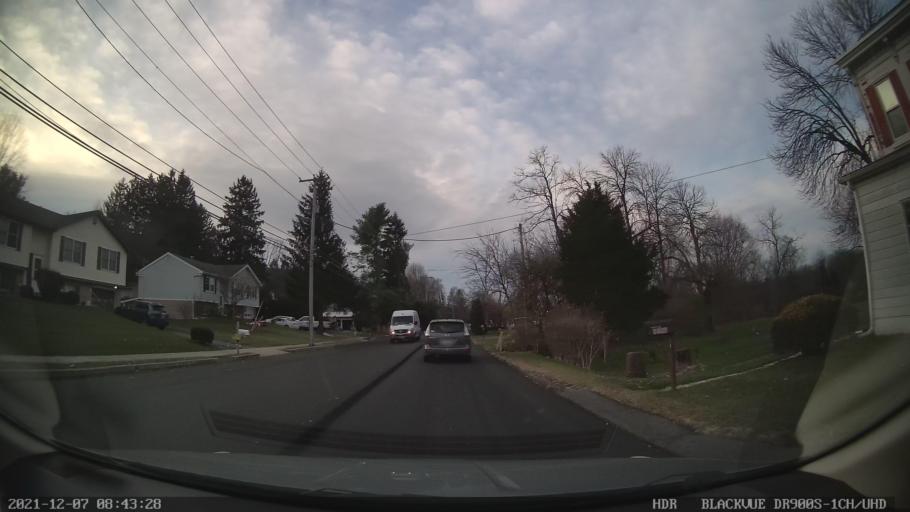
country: US
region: Pennsylvania
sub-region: Berks County
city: Laureldale
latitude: 40.3719
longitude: -75.8981
